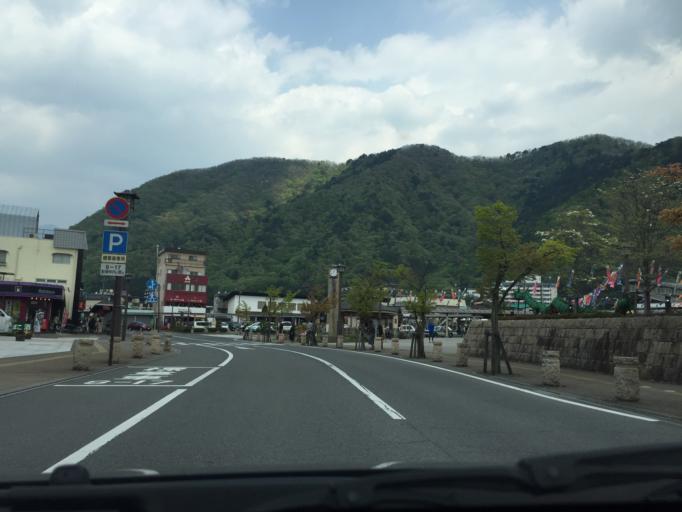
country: JP
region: Tochigi
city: Imaichi
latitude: 36.8235
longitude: 139.7158
